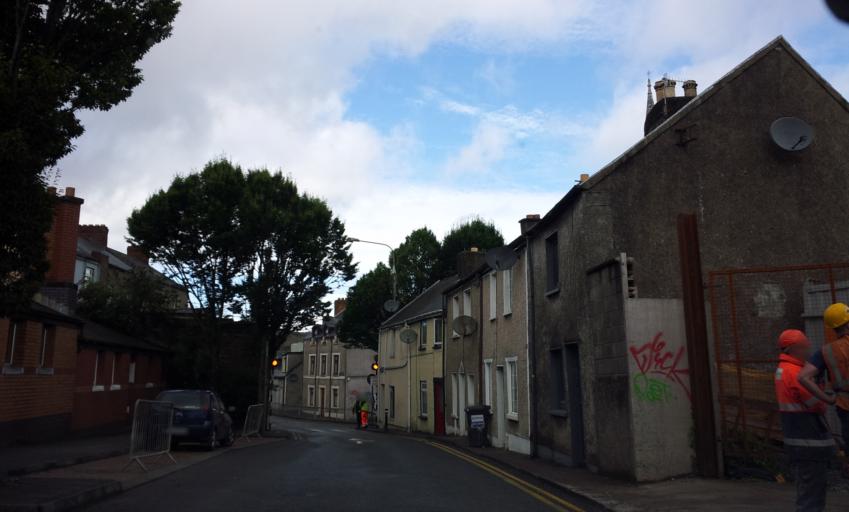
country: IE
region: Munster
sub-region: County Cork
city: Cork
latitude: 51.8936
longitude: -8.4741
